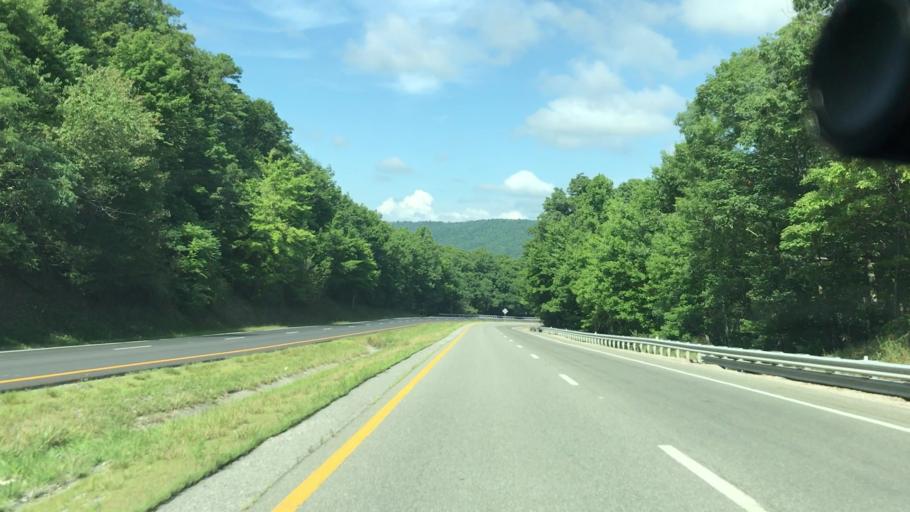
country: US
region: Virginia
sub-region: Montgomery County
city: Blacksburg
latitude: 37.2827
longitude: -80.4467
